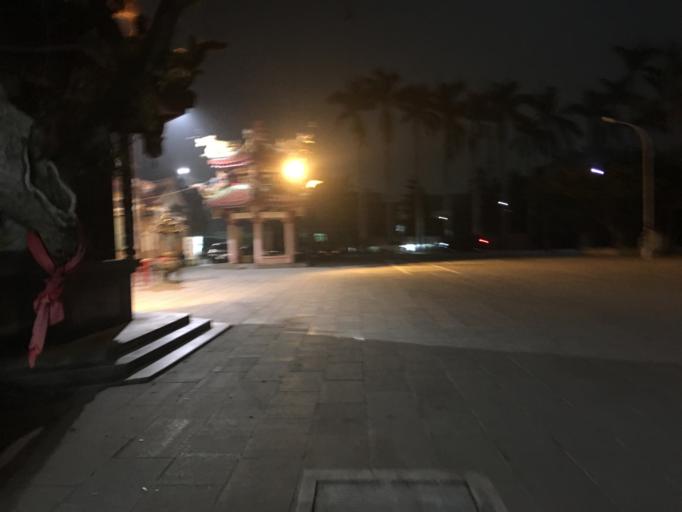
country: TW
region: Taiwan
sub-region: Miaoli
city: Miaoli
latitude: 24.6791
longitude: 120.8852
